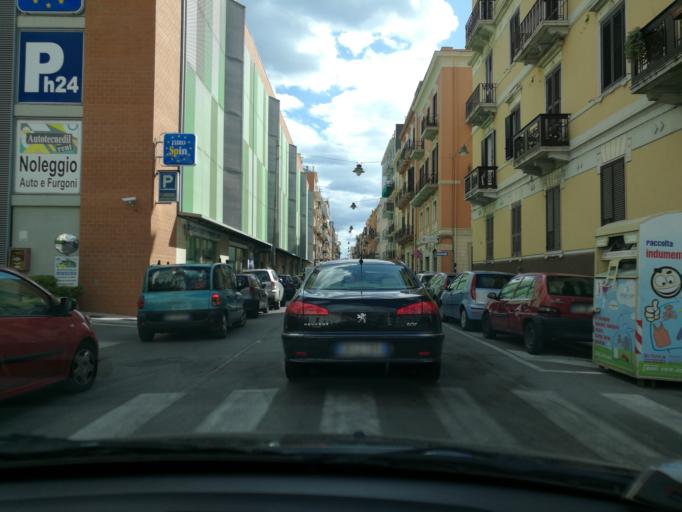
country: IT
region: Apulia
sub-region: Provincia di Bari
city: Bari
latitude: 41.1269
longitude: 16.8572
